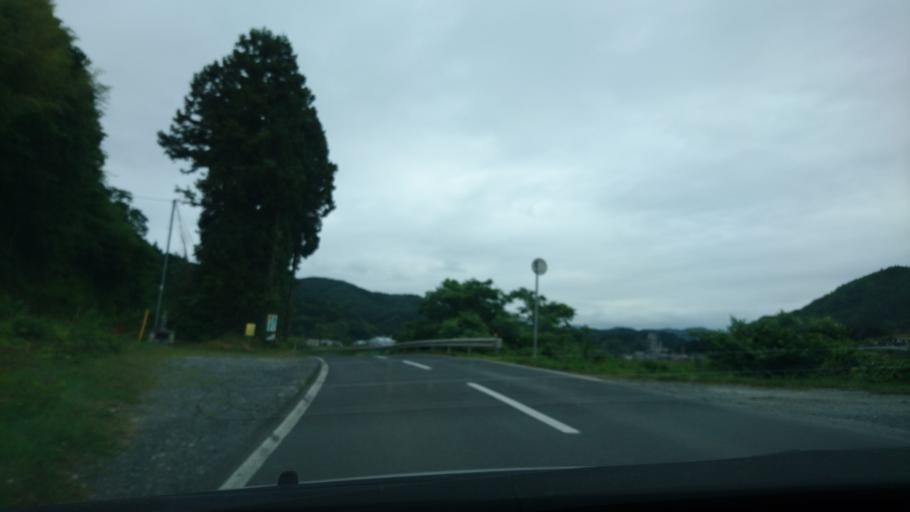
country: JP
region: Iwate
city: Ichinoseki
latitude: 38.9698
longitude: 141.2404
